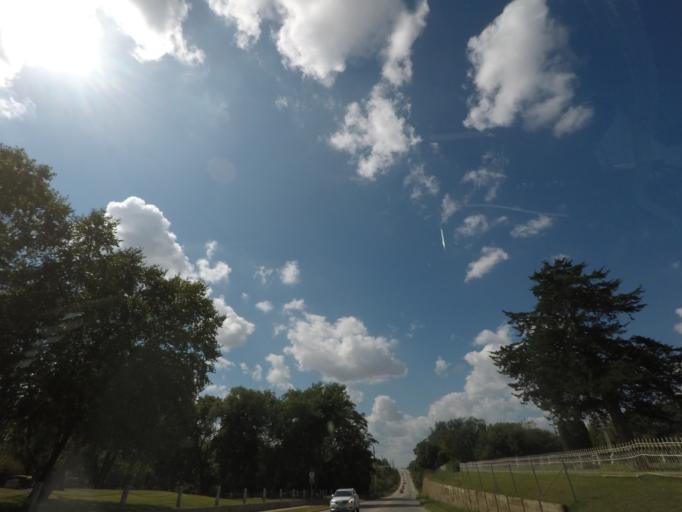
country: US
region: Iowa
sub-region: Story County
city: Nevada
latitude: 42.0228
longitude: -93.4637
